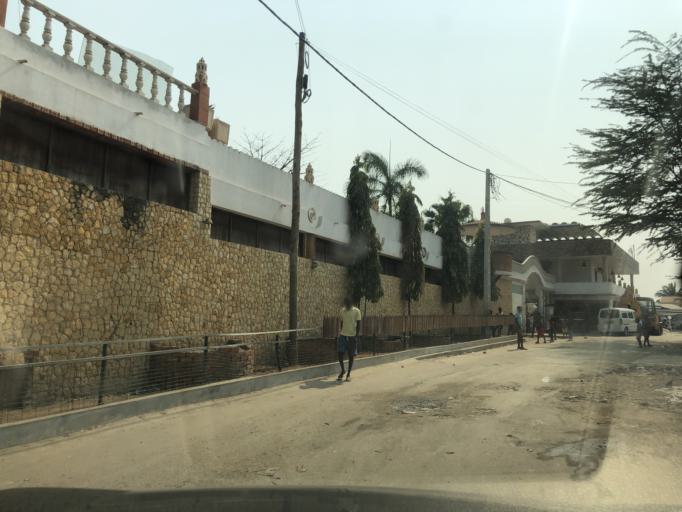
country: AO
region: Luanda
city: Luanda
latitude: -8.9035
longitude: 13.1635
